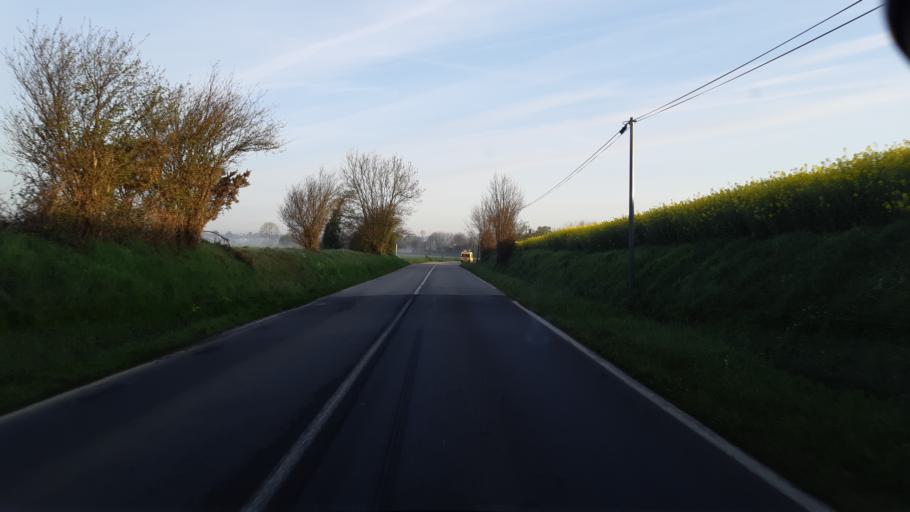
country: FR
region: Lower Normandy
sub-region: Departement de la Manche
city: Agneaux
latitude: 49.0538
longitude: -1.1312
